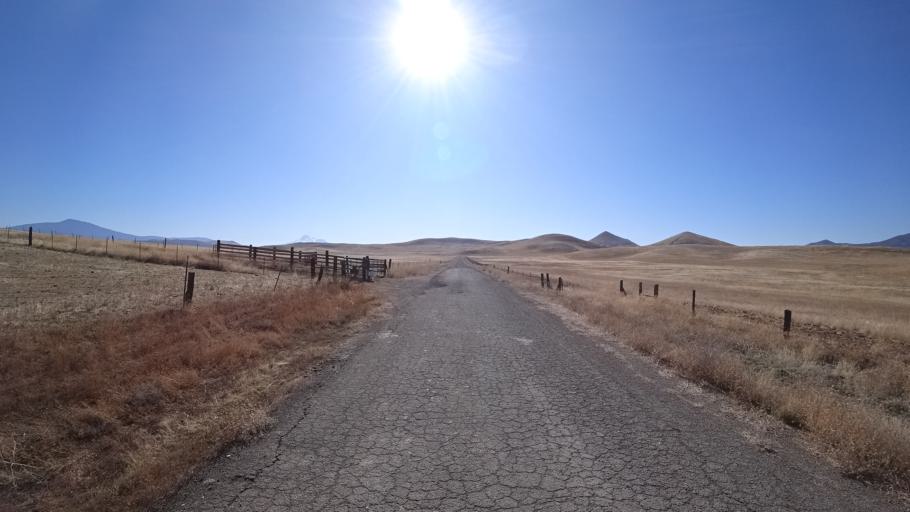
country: US
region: California
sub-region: Siskiyou County
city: Montague
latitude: 41.8446
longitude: -122.4596
